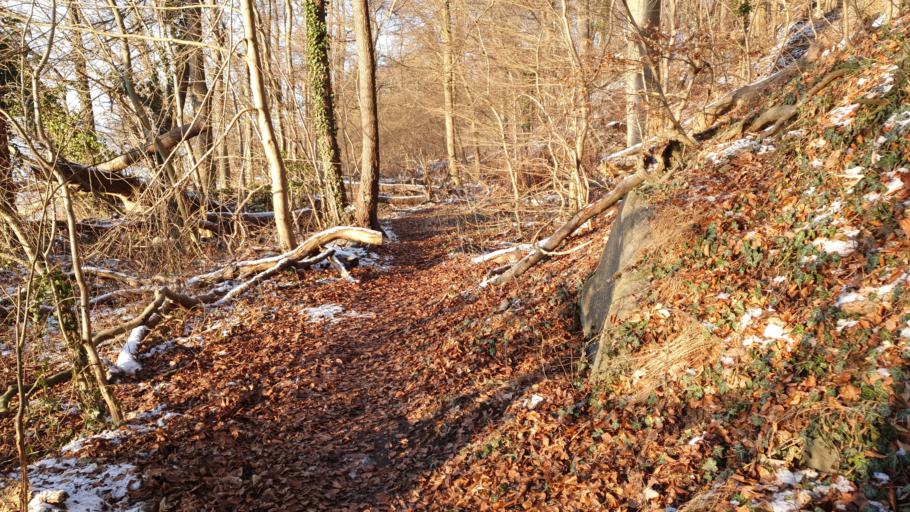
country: DE
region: Mecklenburg-Vorpommern
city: Leezen
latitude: 53.6557
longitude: 11.4852
